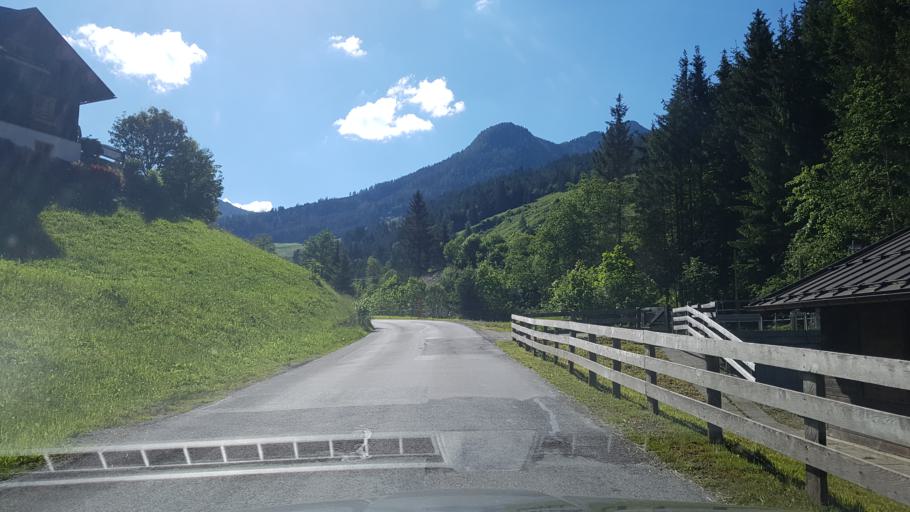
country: AT
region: Salzburg
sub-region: Politischer Bezirk Sankt Johann im Pongau
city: Huttschlag
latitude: 47.2363
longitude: 13.2332
